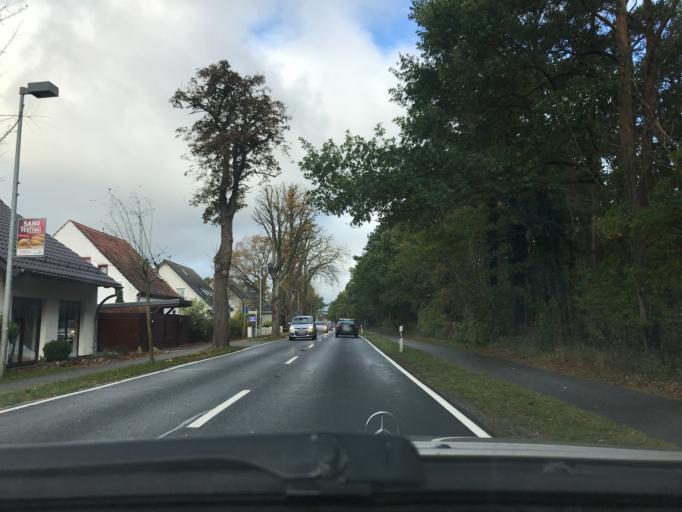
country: DE
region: Mecklenburg-Vorpommern
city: Karlshagen
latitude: 54.1098
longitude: 13.8396
